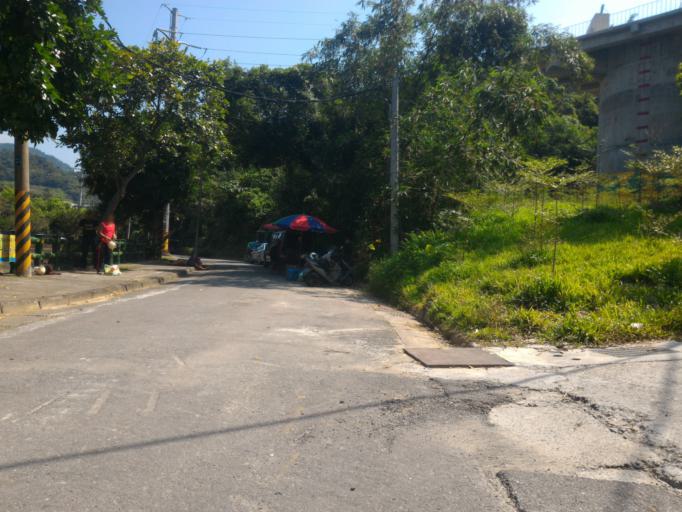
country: TW
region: Taipei
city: Taipei
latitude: 25.0398
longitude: 121.6144
